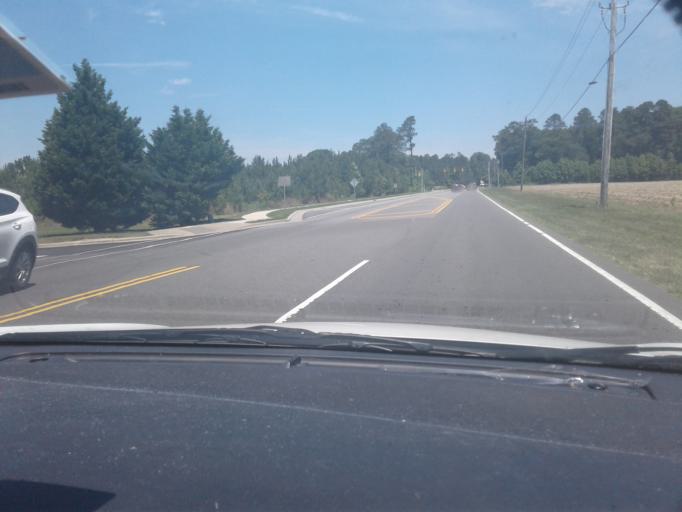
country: US
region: North Carolina
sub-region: Wake County
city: Fuquay-Varina
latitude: 35.5959
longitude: -78.7743
